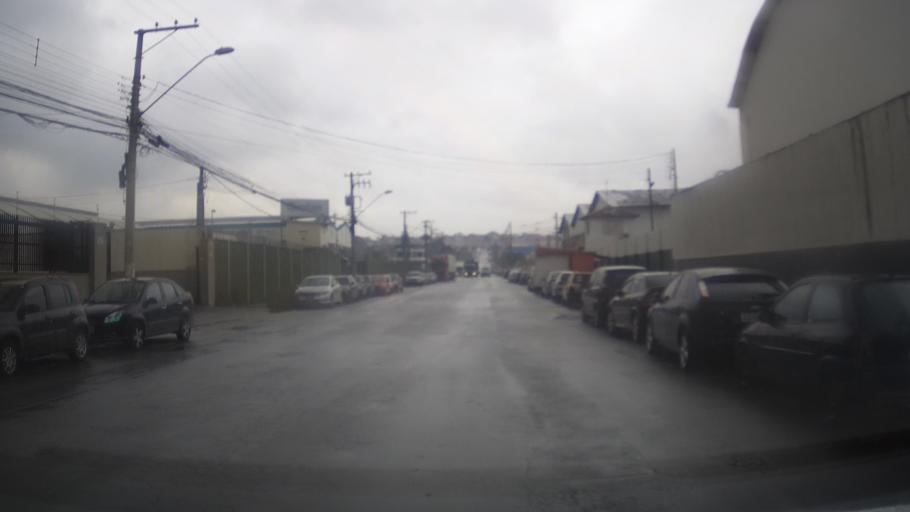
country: BR
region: Sao Paulo
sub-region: Guarulhos
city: Guarulhos
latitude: -23.4414
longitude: -46.4983
